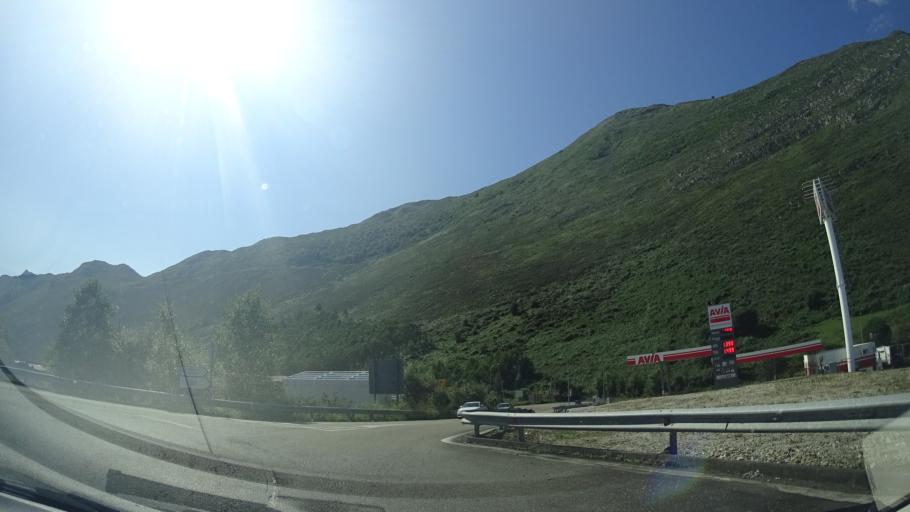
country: ES
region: Asturias
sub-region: Province of Asturias
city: Ribadesella
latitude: 43.4364
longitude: -5.0146
